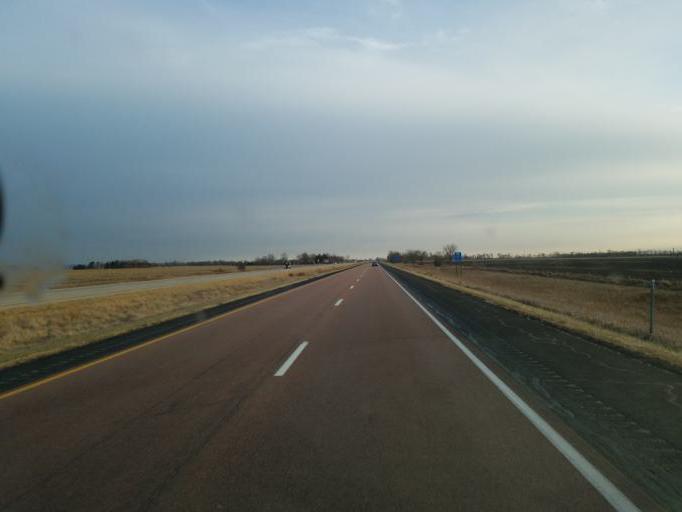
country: US
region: Iowa
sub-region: Monona County
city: Onawa
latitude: 42.0044
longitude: -96.1160
